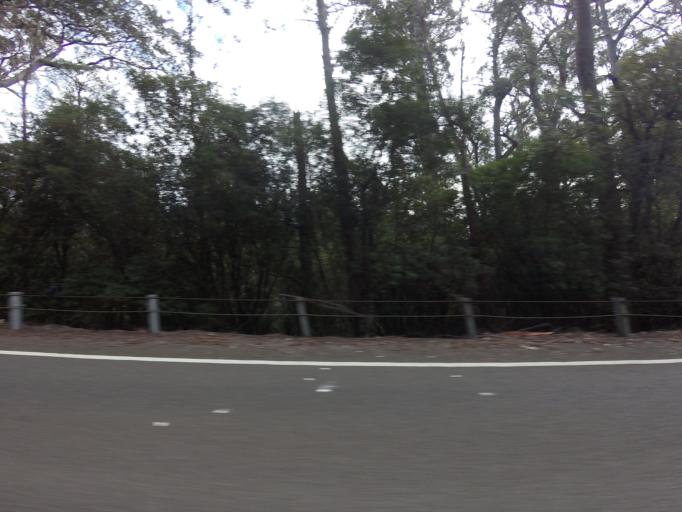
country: AU
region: Tasmania
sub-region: Meander Valley
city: Deloraine
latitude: -41.6527
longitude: 146.7238
